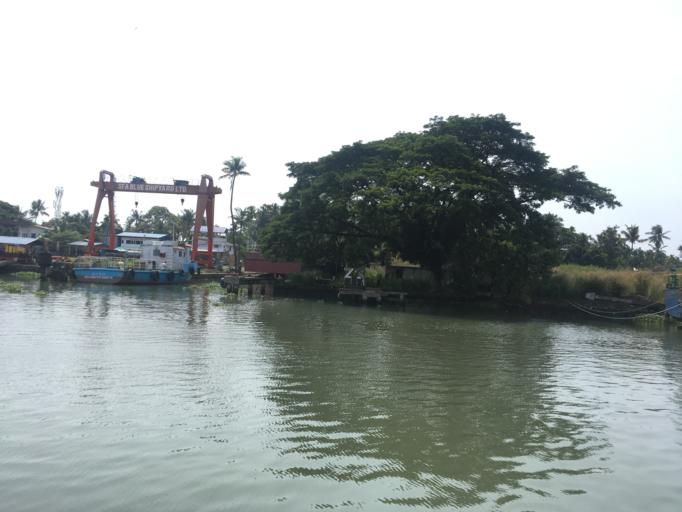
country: IN
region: Kerala
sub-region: Ernakulam
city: Cochin
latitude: 9.9765
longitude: 76.2440
